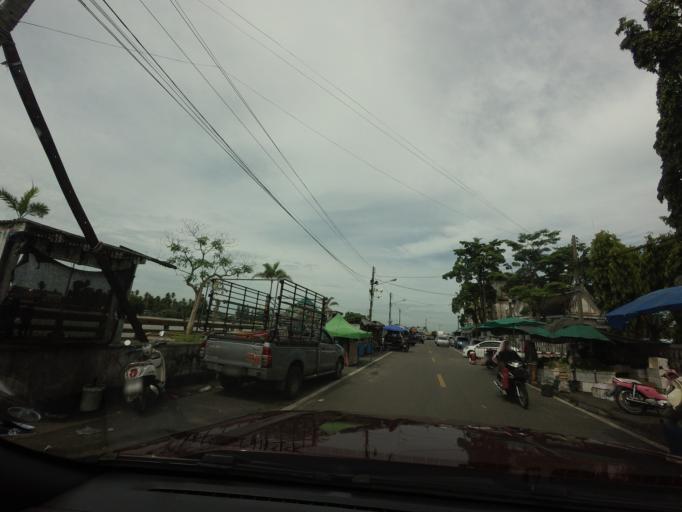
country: TH
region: Narathiwat
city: Tak Bai
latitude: 6.2349
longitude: 102.0891
